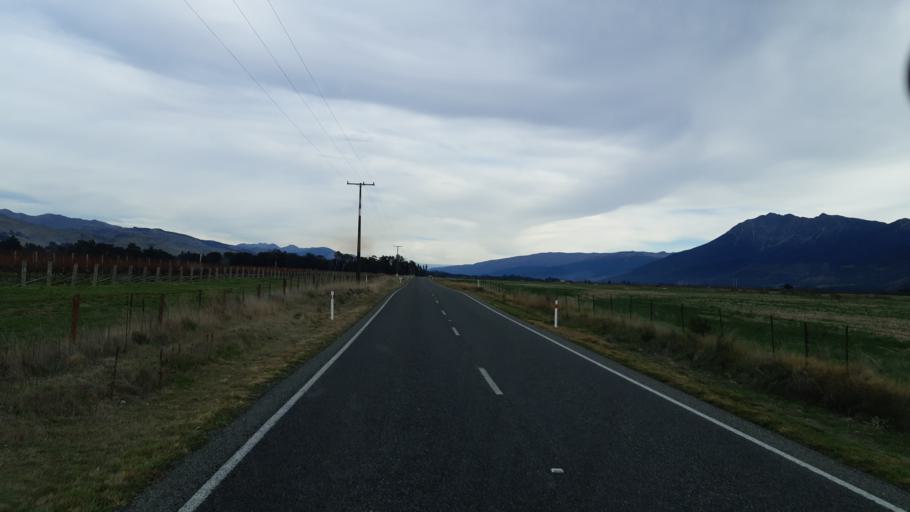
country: NZ
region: Tasman
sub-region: Tasman District
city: Richmond
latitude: -41.6148
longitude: 173.3833
